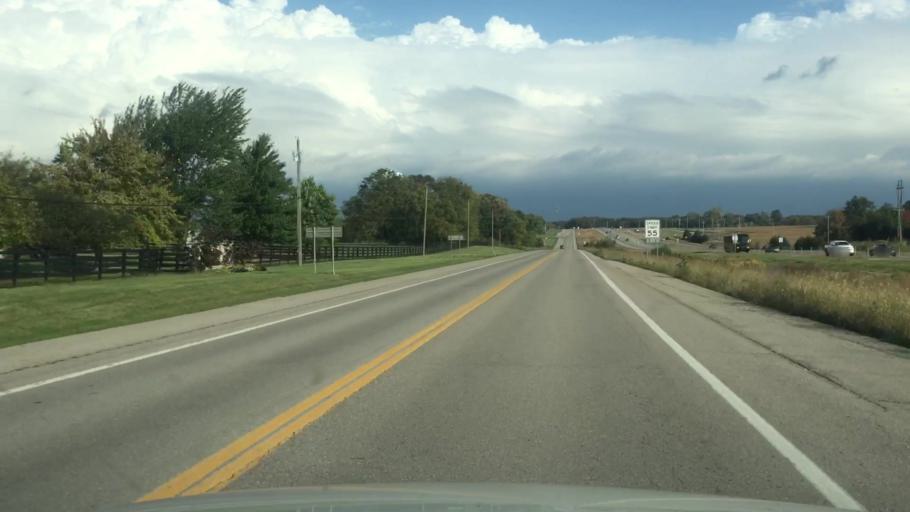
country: US
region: Missouri
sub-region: Boone County
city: Ashland
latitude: 38.8628
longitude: -92.2506
